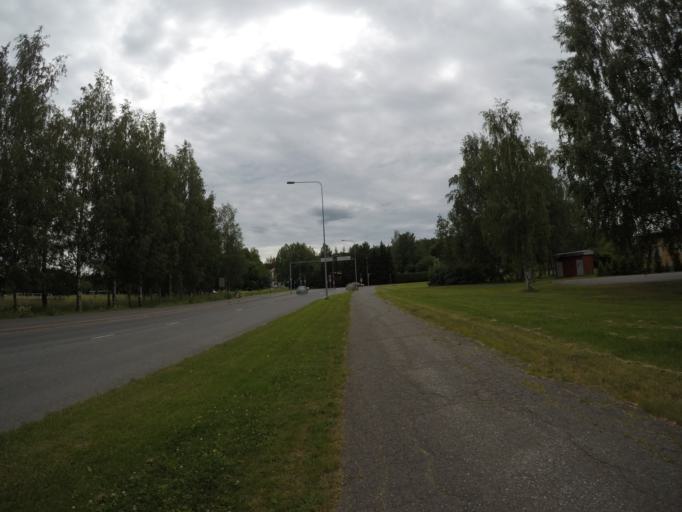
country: FI
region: Haeme
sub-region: Haemeenlinna
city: Haemeenlinna
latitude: 61.0039
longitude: 24.4262
